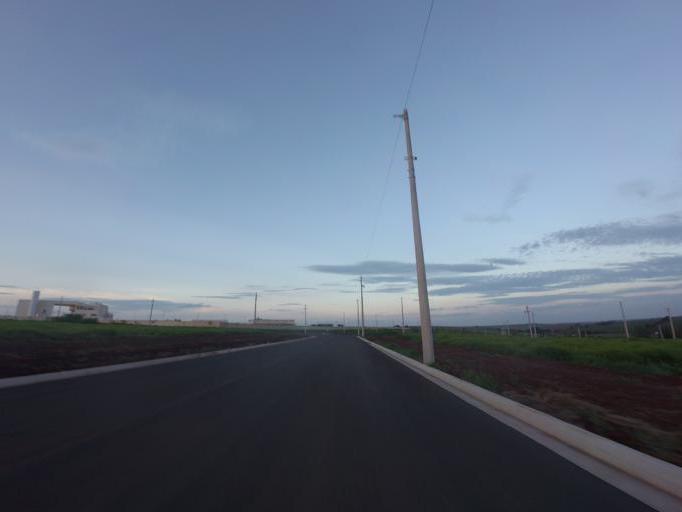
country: BR
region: Sao Paulo
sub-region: Piracicaba
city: Piracicaba
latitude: -22.7642
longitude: -47.5838
